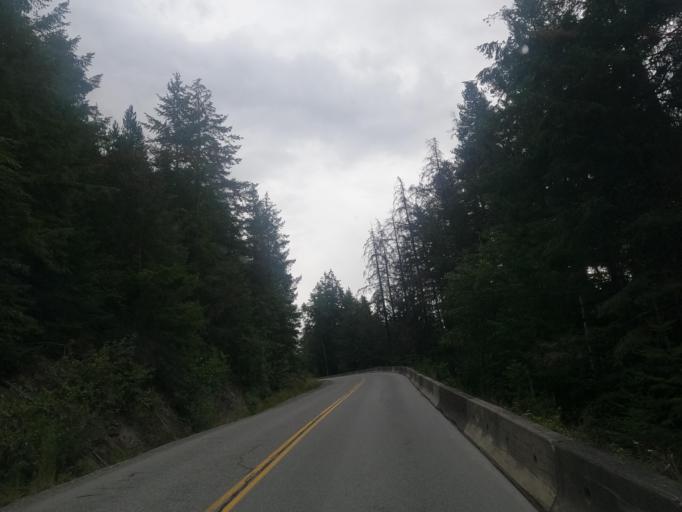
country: CA
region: British Columbia
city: Pemberton
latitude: 50.3013
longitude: -122.5865
